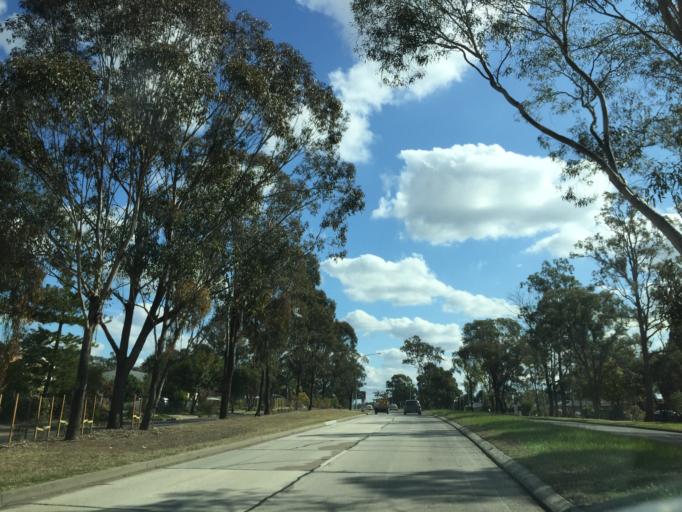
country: AU
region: New South Wales
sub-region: Blacktown
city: Quakers Hill
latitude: -33.7443
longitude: 150.8749
